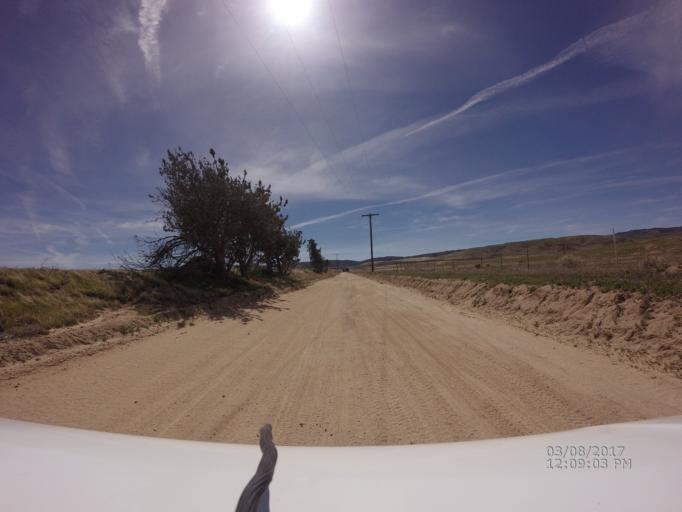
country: US
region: California
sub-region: Los Angeles County
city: Green Valley
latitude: 34.7304
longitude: -118.4287
